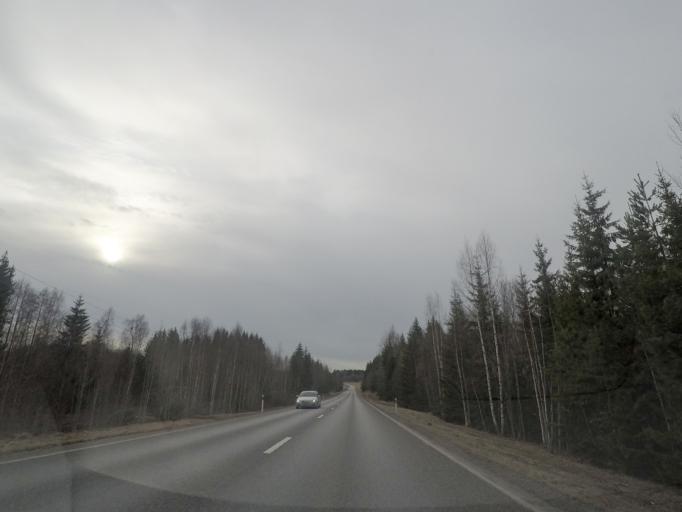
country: SE
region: Vaestmanland
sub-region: Skinnskattebergs Kommun
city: Skinnskatteberg
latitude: 59.7989
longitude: 15.8650
